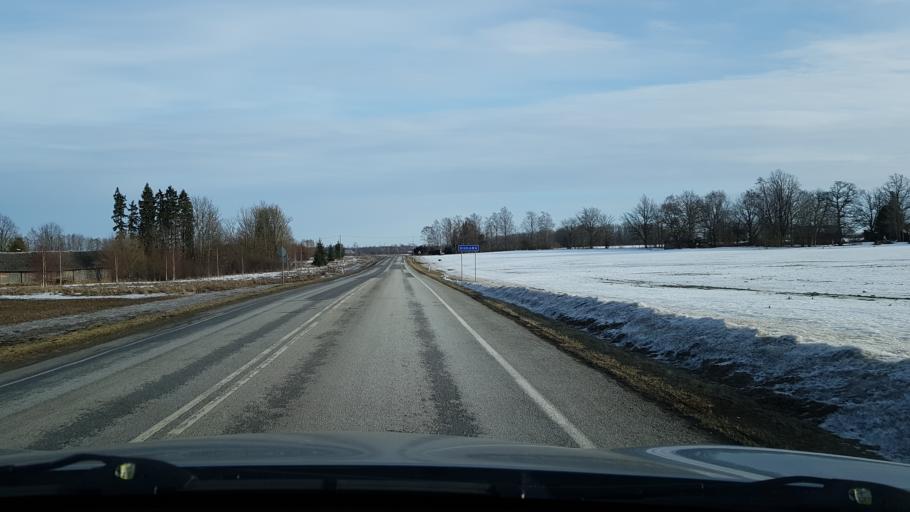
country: EE
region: Viljandimaa
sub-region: Viljandi linn
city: Viljandi
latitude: 58.3555
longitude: 25.4350
